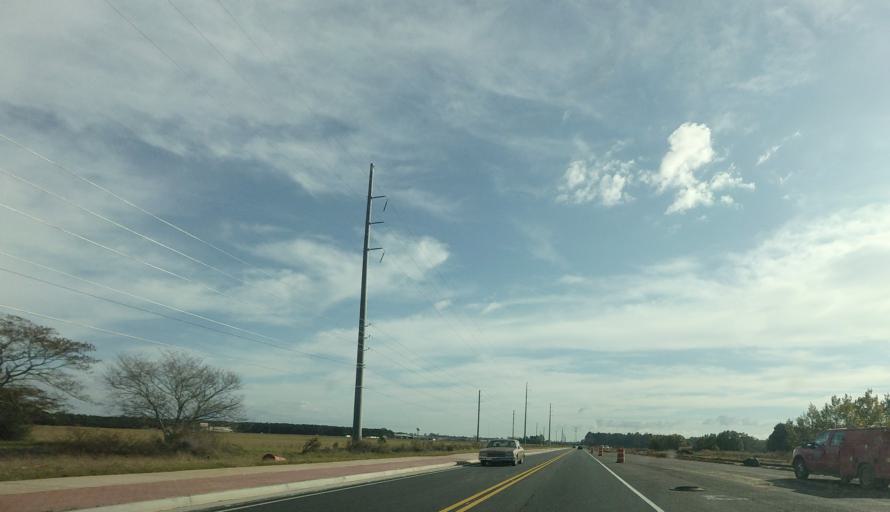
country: US
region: Georgia
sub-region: Houston County
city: Centerville
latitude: 32.5468
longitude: -83.7045
